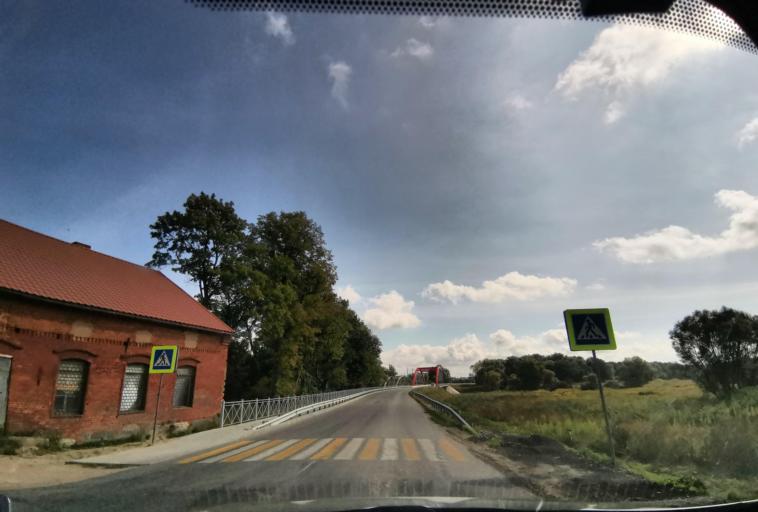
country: RU
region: Kaliningrad
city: Chernyakhovsk
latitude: 54.6601
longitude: 21.8070
